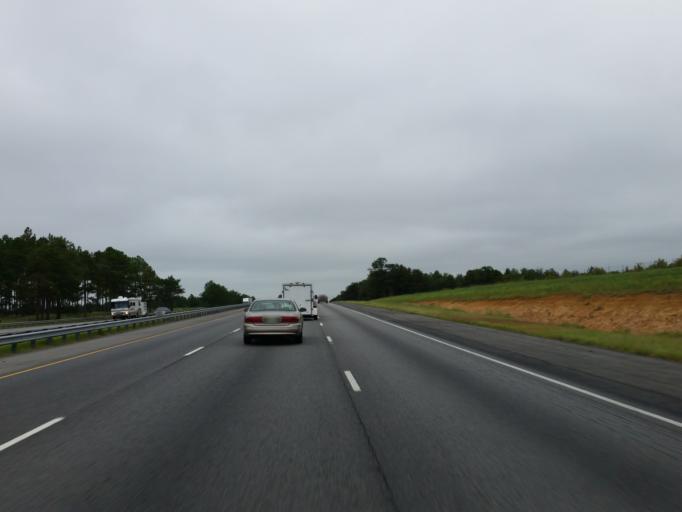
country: US
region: Georgia
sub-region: Crisp County
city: Cordele
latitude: 31.8739
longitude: -83.7256
